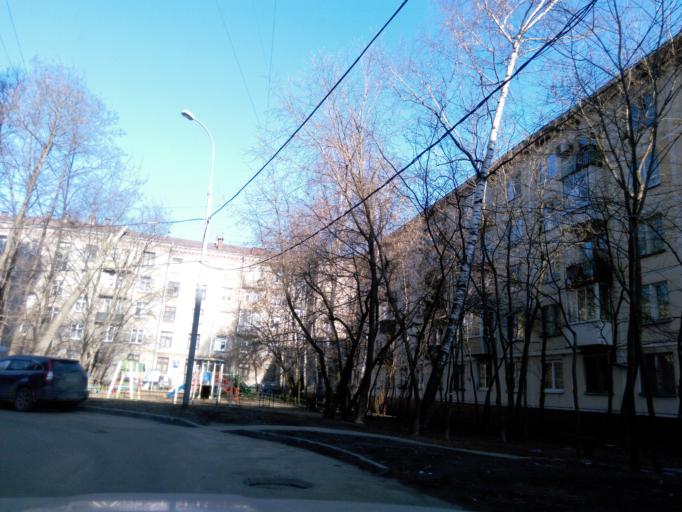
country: RU
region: Moskovskaya
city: Koptevo
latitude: 55.8181
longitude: 37.5250
